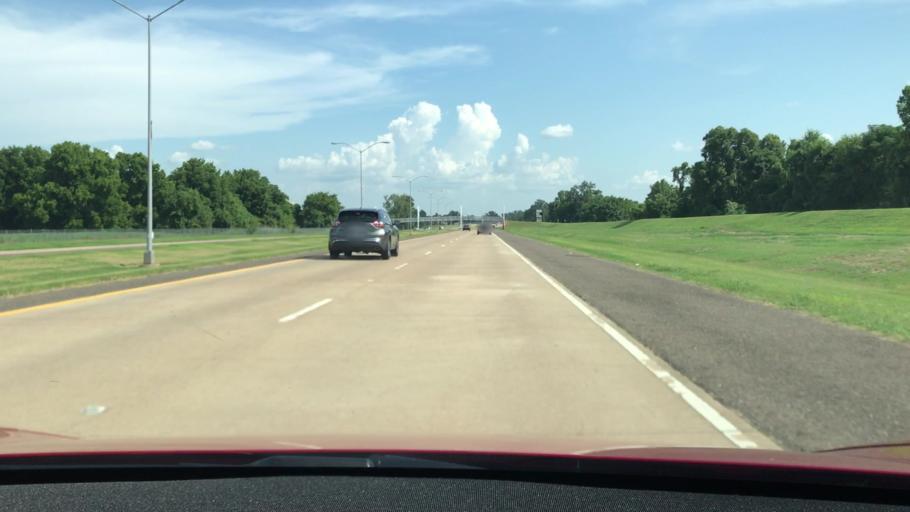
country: US
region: Louisiana
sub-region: Bossier Parish
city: Bossier City
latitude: 32.4734
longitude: -93.6786
